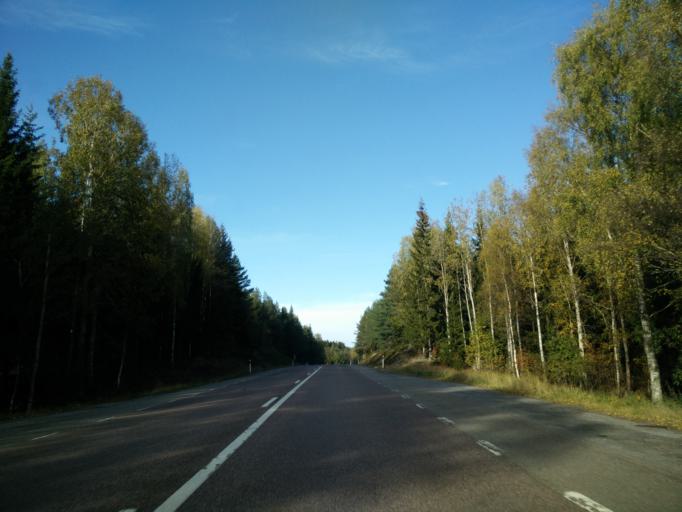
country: SE
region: Gaevleborg
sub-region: Hudiksvalls Kommun
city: Iggesund
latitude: 61.5862
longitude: 17.0258
